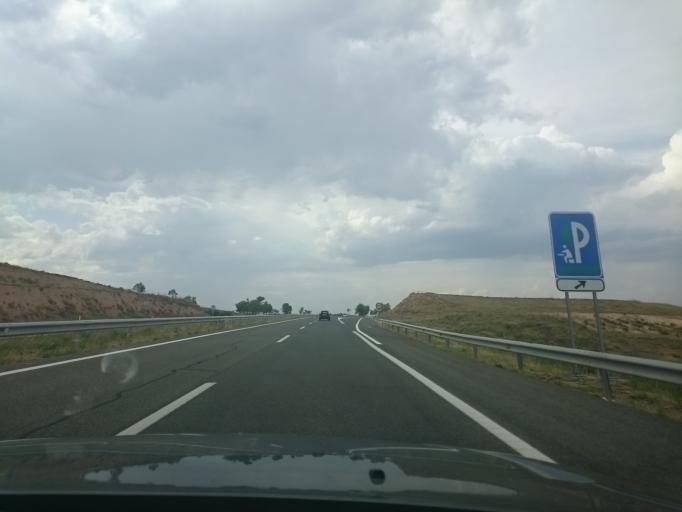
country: ES
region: Navarre
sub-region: Provincia de Navarra
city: Corella
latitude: 42.1618
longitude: -1.8224
